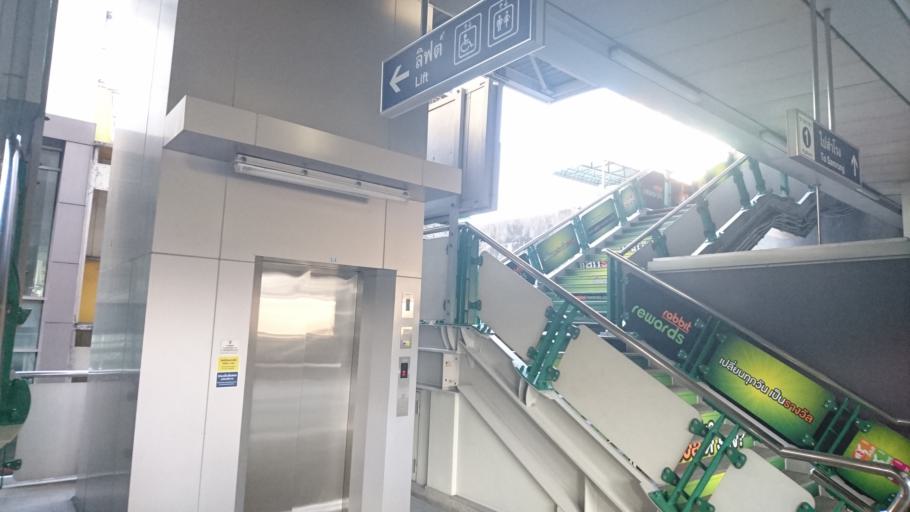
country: TH
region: Bangkok
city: Watthana
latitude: 13.7153
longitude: 100.5913
